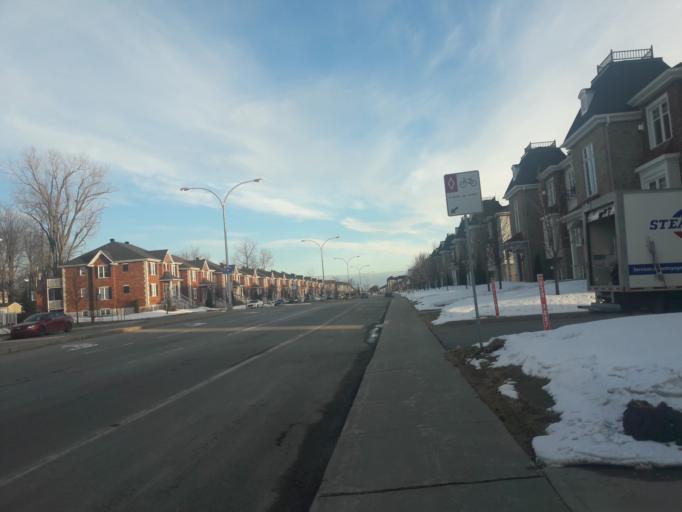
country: CA
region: Quebec
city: Dollard-Des Ormeaux
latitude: 45.5532
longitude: -73.7852
